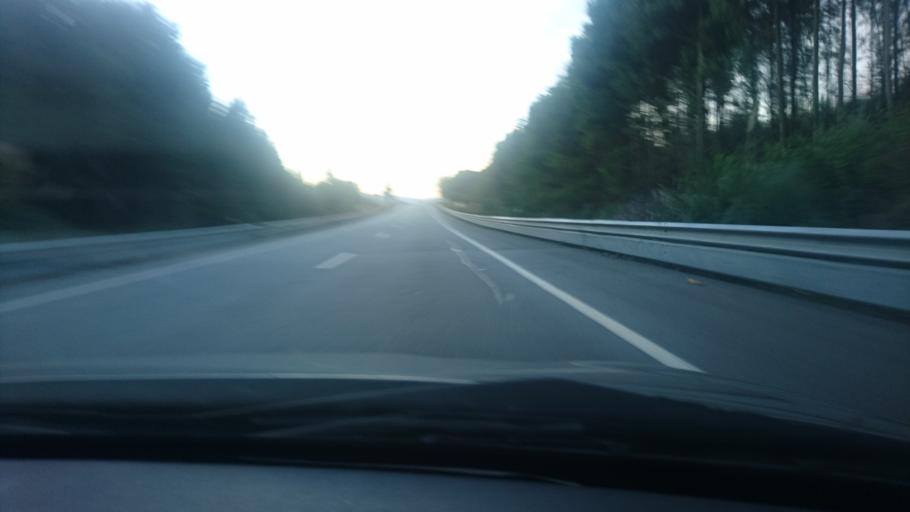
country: PT
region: Aveiro
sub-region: Santa Maria da Feira
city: Arrifana
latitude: 40.9189
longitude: -8.4898
